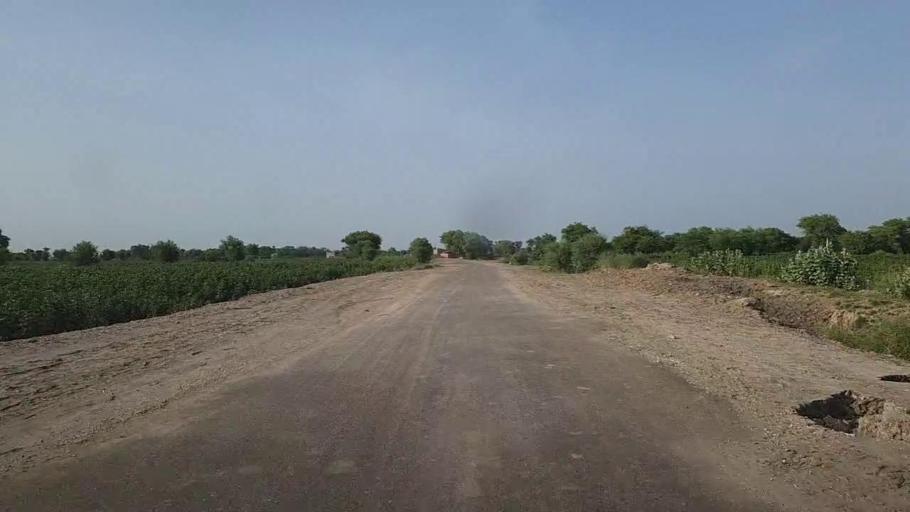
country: PK
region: Sindh
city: Ubauro
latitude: 28.0944
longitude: 69.8451
